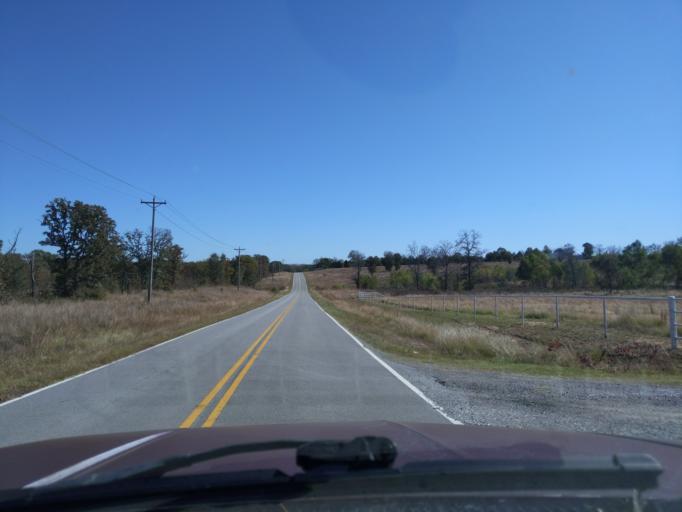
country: US
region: Oklahoma
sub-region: Creek County
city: Bristow
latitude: 35.7118
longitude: -96.3949
